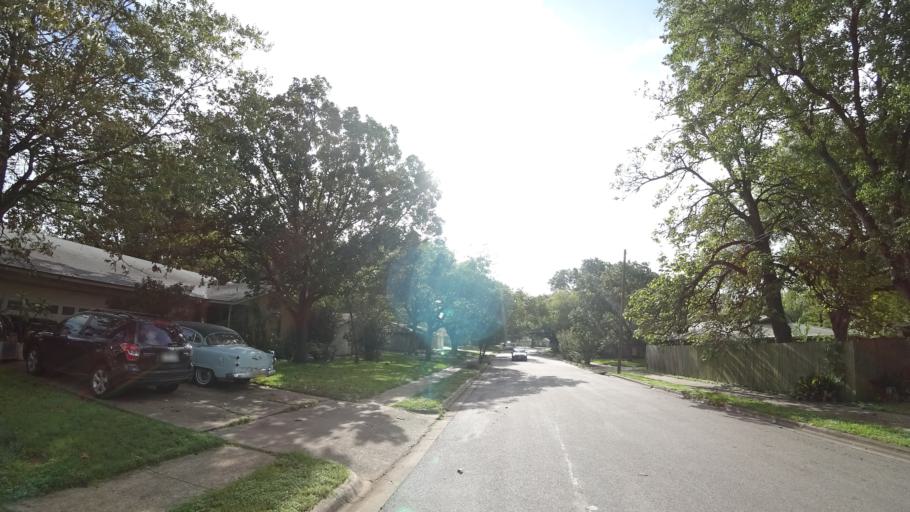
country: US
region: Texas
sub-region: Travis County
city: West Lake Hills
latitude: 30.3499
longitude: -97.7461
